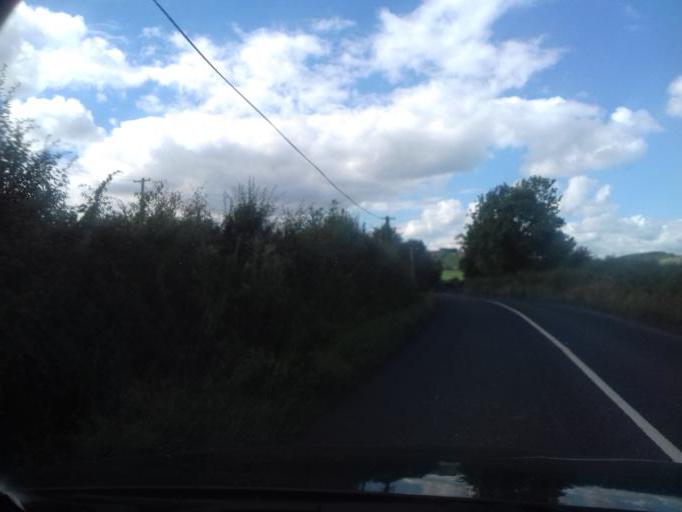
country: IE
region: Munster
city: Carrick-on-Suir
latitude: 52.3860
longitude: -7.4656
